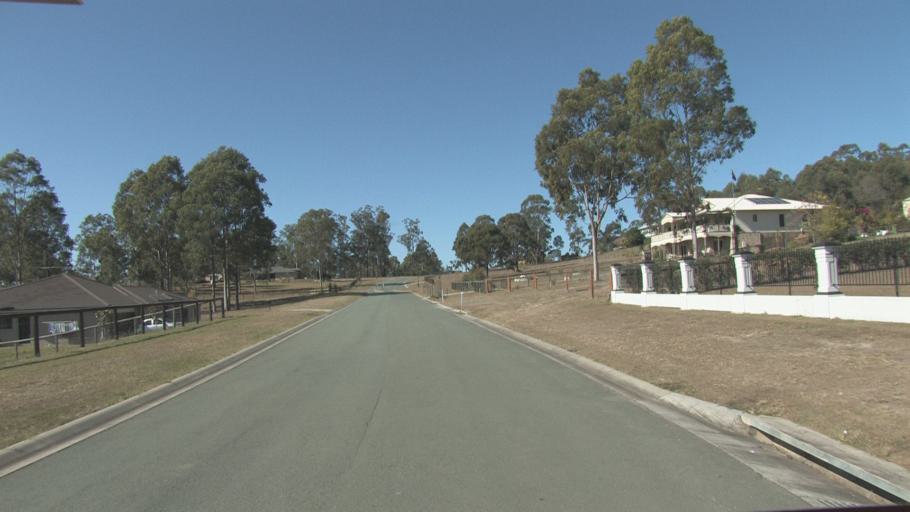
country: AU
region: Queensland
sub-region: Logan
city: Cedar Vale
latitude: -27.8686
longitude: 153.0324
